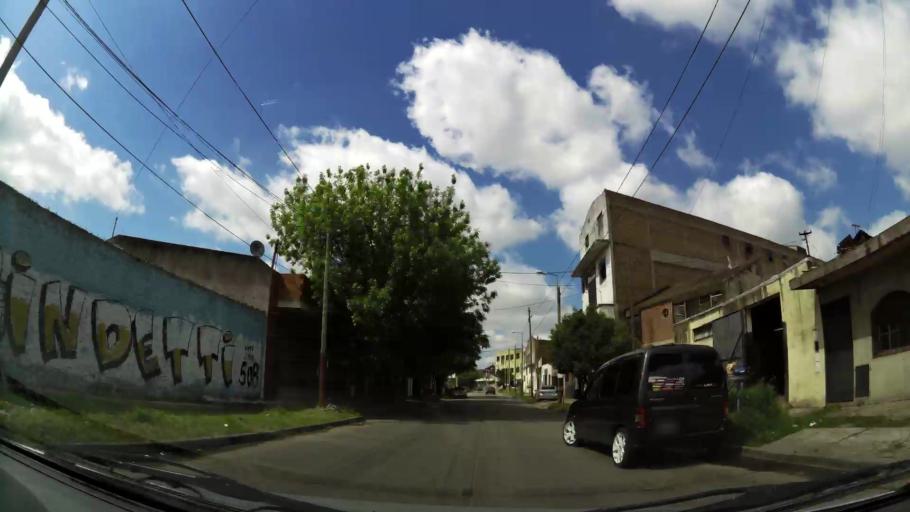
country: AR
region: Buenos Aires
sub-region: Partido de Lanus
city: Lanus
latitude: -34.6801
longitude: -58.4210
